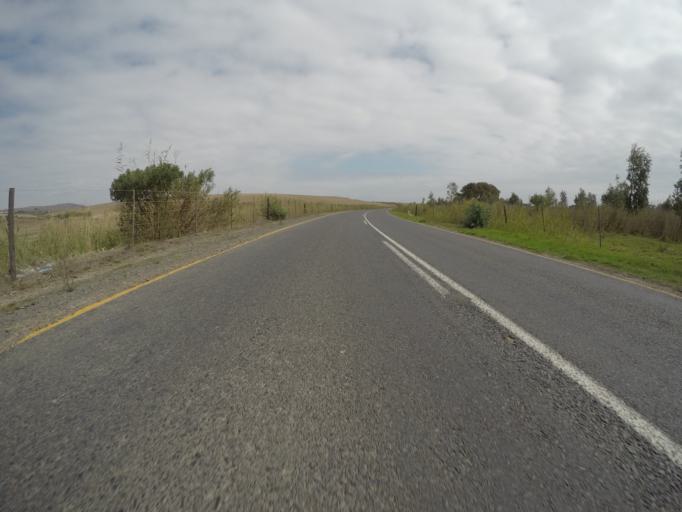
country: ZA
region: Western Cape
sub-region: City of Cape Town
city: Sunset Beach
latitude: -33.7877
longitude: 18.5547
